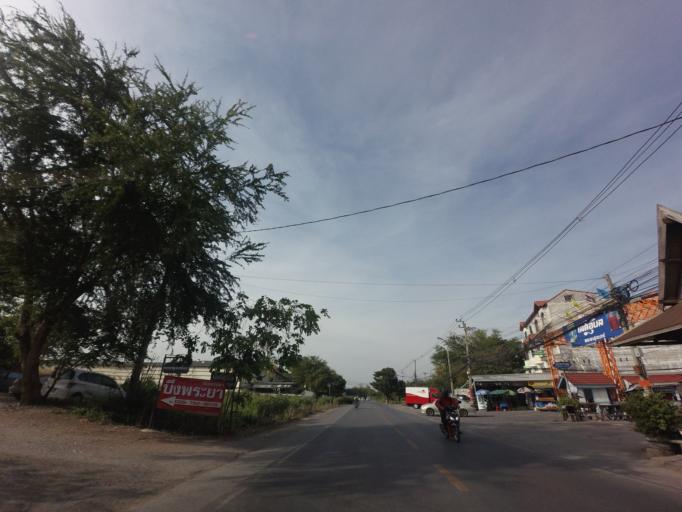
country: TH
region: Bangkok
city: Khan Na Yao
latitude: 13.8708
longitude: 100.6903
